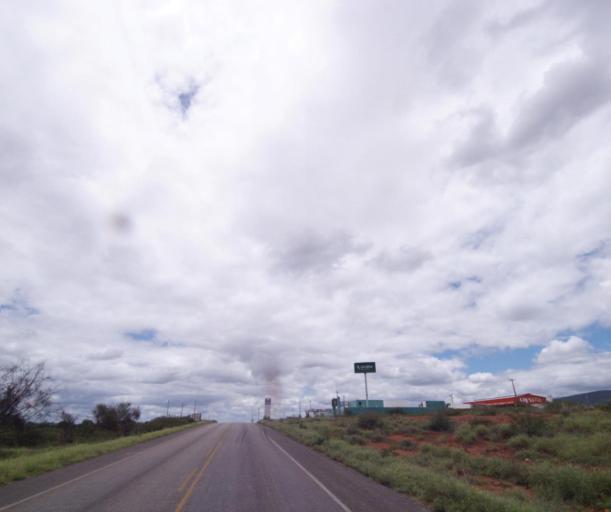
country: BR
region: Bahia
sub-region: Brumado
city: Brumado
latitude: -14.2260
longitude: -41.6741
